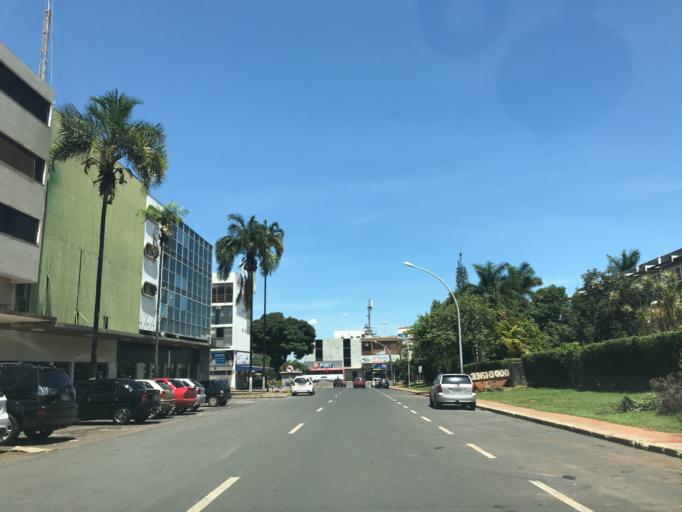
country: BR
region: Federal District
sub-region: Brasilia
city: Brasilia
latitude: -15.7816
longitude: -47.8891
